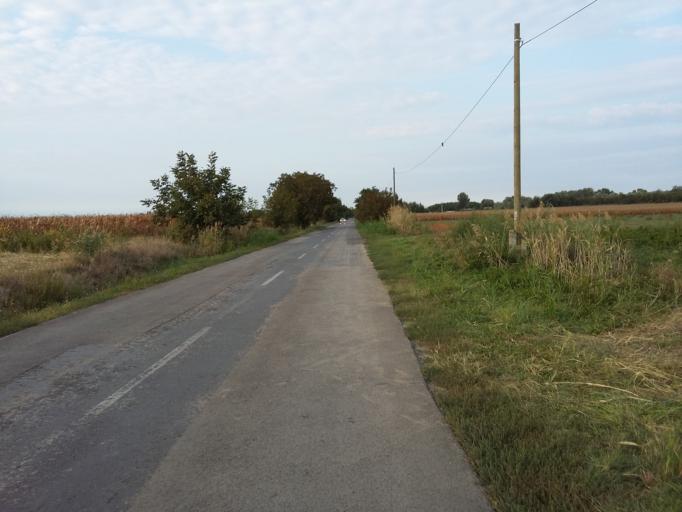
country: HU
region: Csongrad
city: Szeged
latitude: 46.2124
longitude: 20.1086
